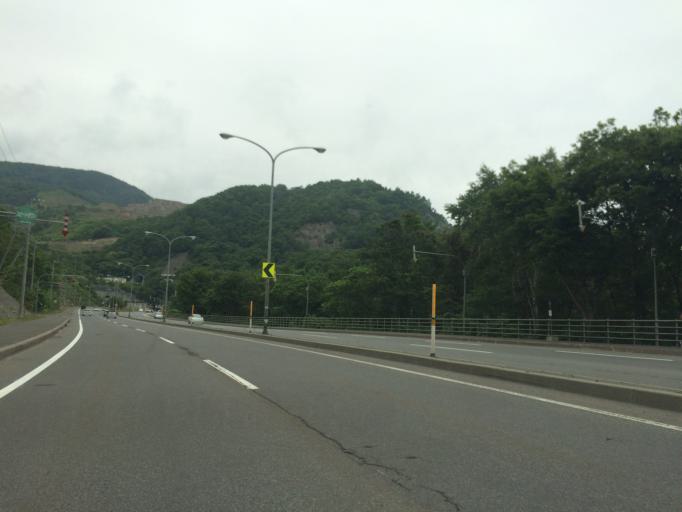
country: JP
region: Hokkaido
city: Otaru
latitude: 43.1627
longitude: 141.1042
